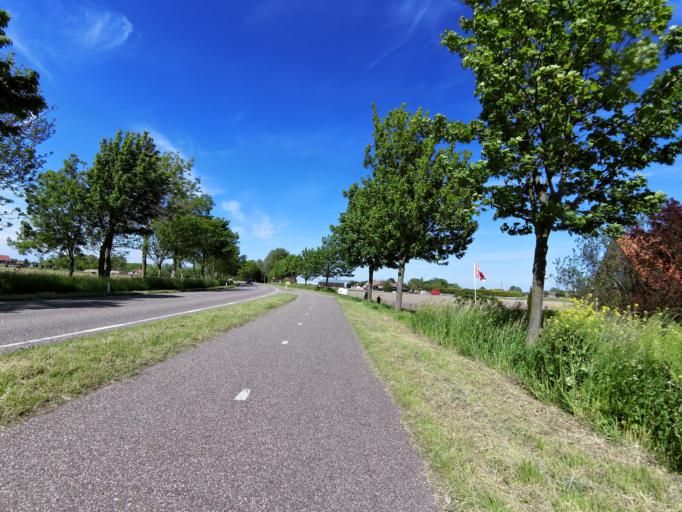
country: NL
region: South Holland
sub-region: Gemeente Hellevoetsluis
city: Nieuwenhoorn
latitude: 51.8647
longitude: 4.1597
